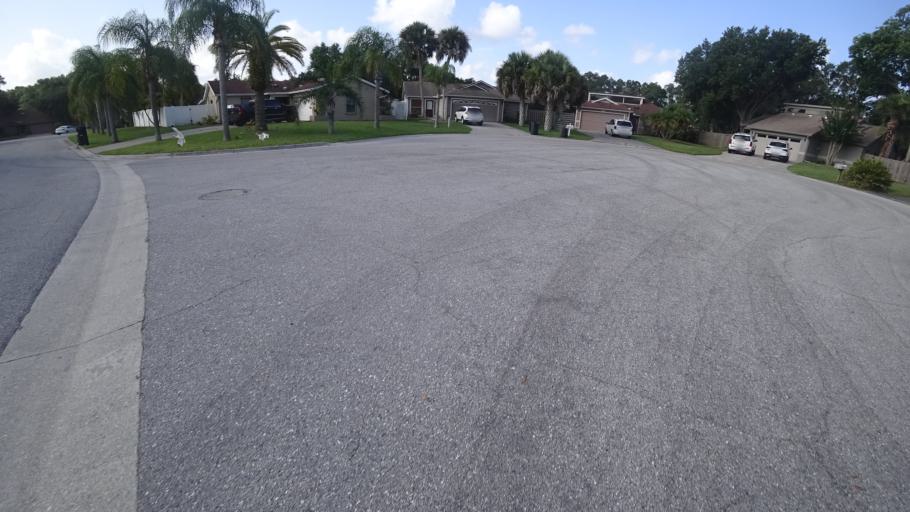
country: US
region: Florida
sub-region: Sarasota County
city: North Sarasota
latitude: 27.3932
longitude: -82.5030
